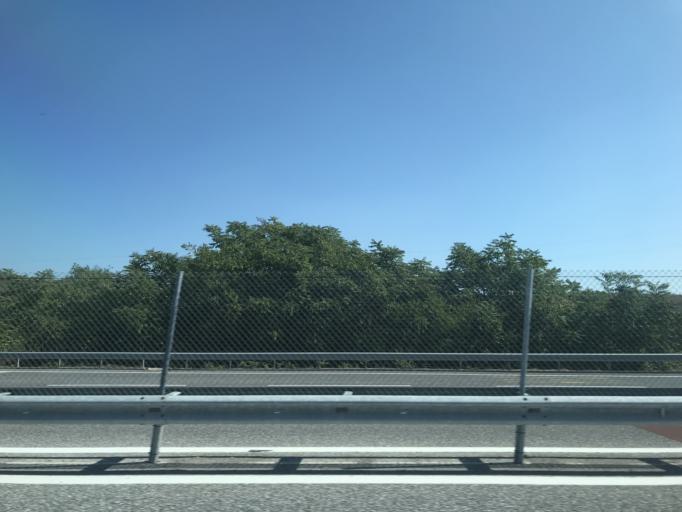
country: TR
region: Kirklareli
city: Luleburgaz
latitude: 41.4446
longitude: 27.3884
